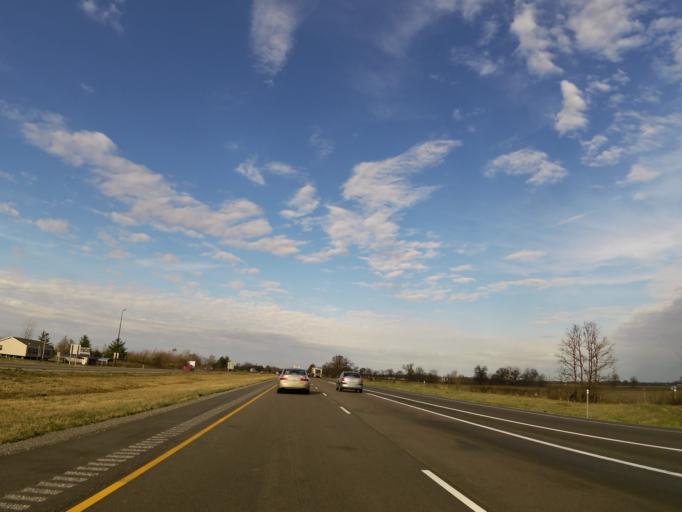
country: US
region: Illinois
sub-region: Washington County
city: Okawville
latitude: 38.4414
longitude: -89.5331
